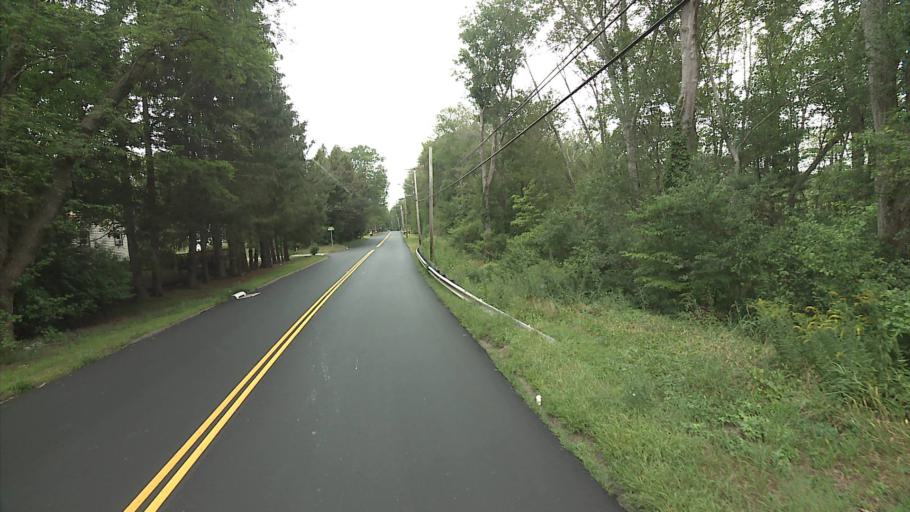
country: US
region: Connecticut
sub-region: New London County
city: Colchester
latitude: 41.5853
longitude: -72.3375
